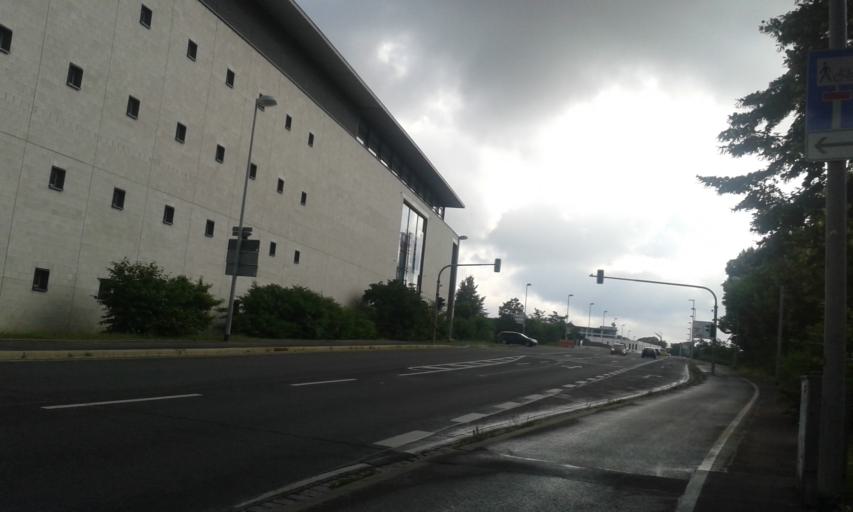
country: DE
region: Bavaria
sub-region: Upper Franconia
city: Bamberg
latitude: 49.9007
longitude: 10.8778
